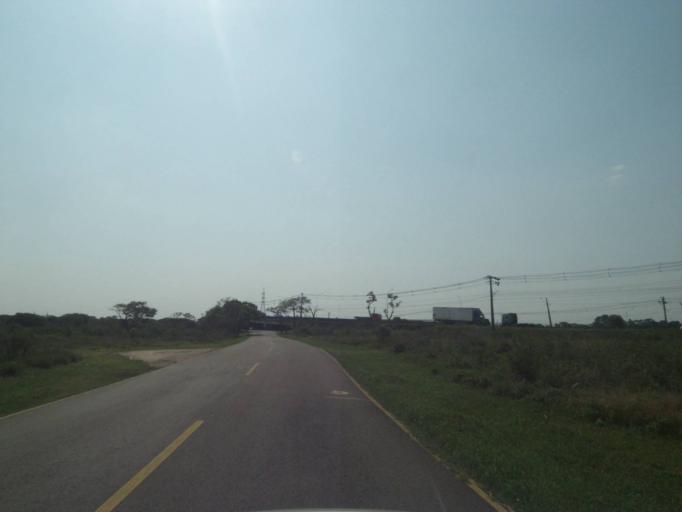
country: BR
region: Parana
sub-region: Sao Jose Dos Pinhais
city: Sao Jose dos Pinhais
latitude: -25.5269
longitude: -49.2242
